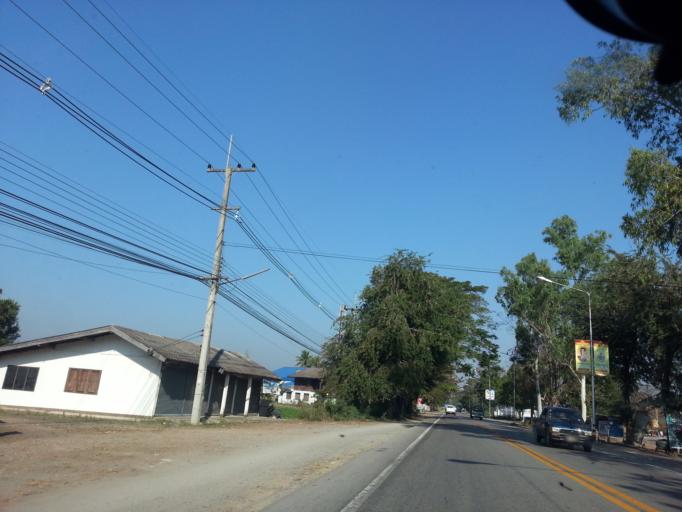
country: TH
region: Chiang Mai
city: Mae Taeng
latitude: 19.0407
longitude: 98.9691
